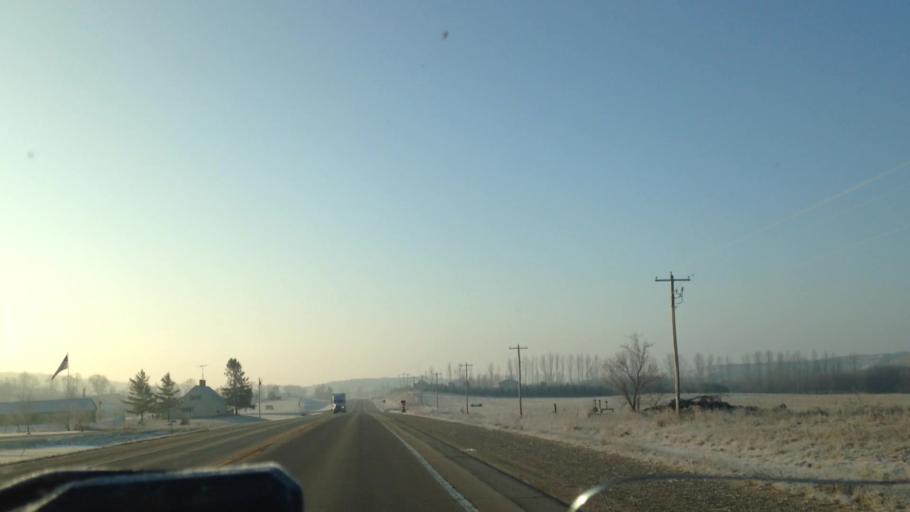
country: US
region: Wisconsin
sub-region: Dodge County
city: Mayville
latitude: 43.4773
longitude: -88.5426
